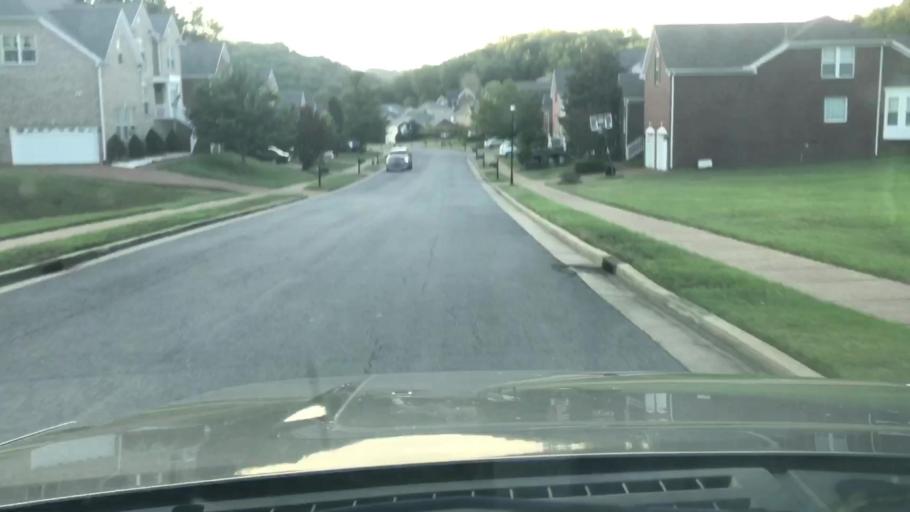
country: US
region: Tennessee
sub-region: Davidson County
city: Belle Meade
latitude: 36.1141
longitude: -86.9282
